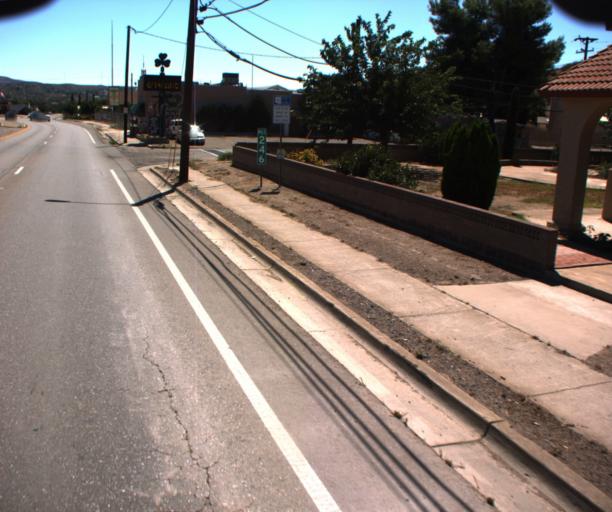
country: US
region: Arizona
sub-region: Gila County
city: Claypool
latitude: 33.4106
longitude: -110.8461
